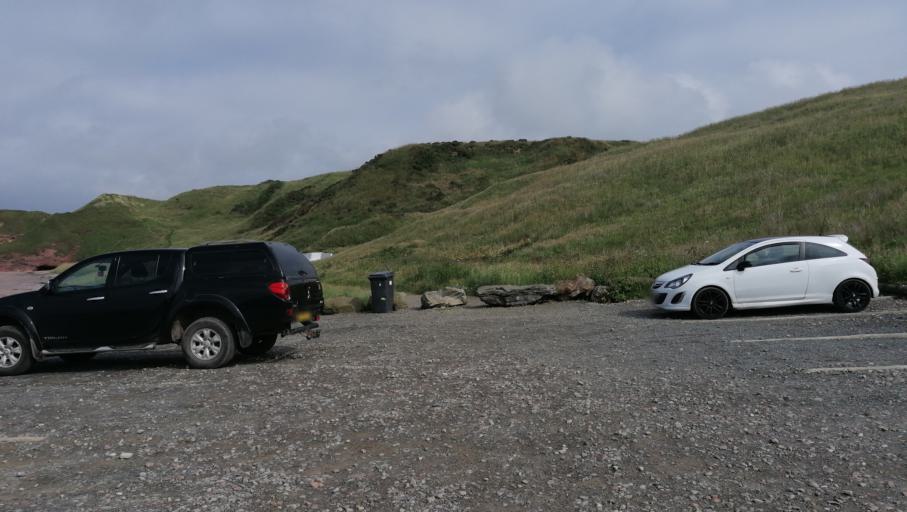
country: GB
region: Scotland
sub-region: Aberdeenshire
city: Rosehearty
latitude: 57.6711
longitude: -2.1927
